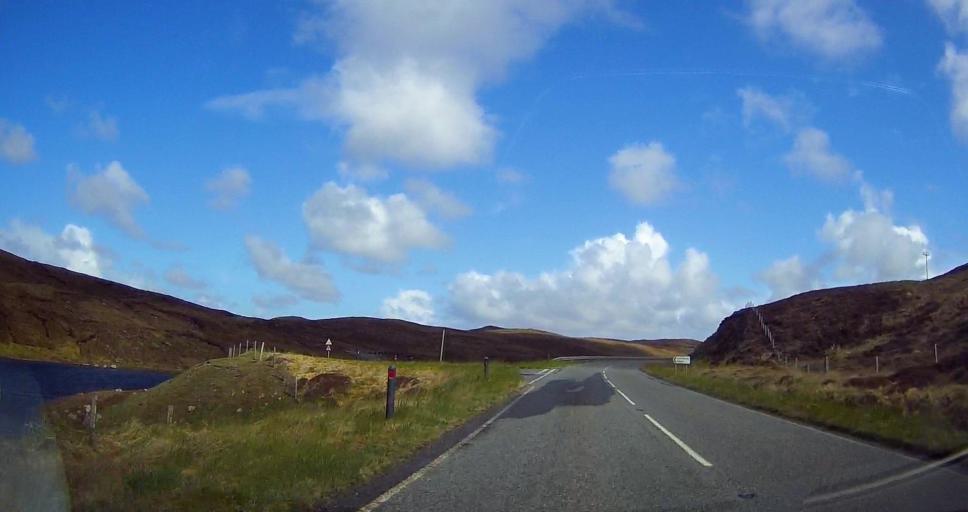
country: GB
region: Scotland
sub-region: Shetland Islands
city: Lerwick
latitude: 60.4384
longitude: -1.3975
